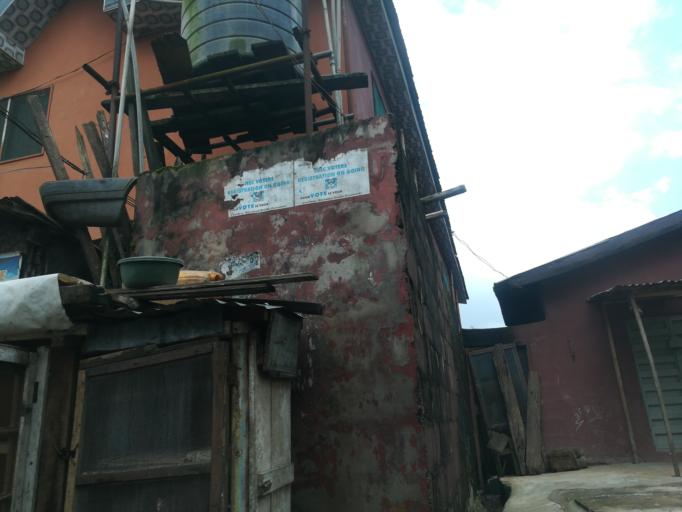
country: NG
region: Lagos
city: Mushin
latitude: 6.5315
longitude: 3.3632
